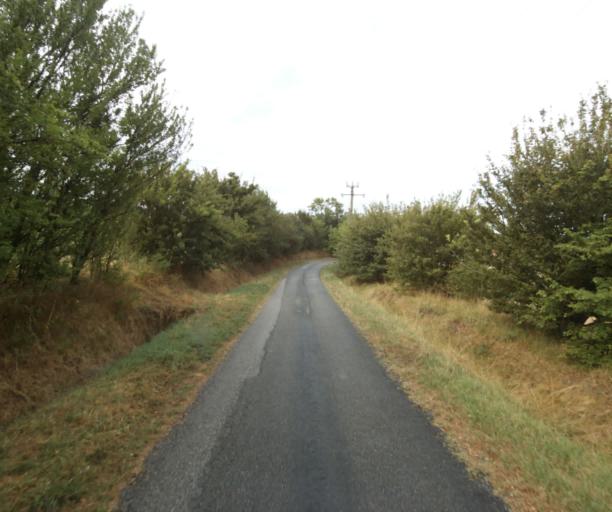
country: FR
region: Midi-Pyrenees
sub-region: Departement de la Haute-Garonne
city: Revel
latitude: 43.4274
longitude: 1.9634
